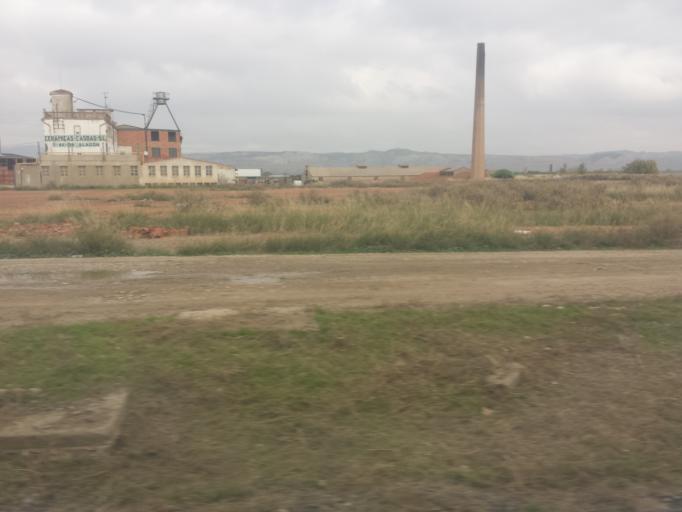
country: ES
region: Aragon
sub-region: Provincia de Zaragoza
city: Alagon
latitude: 41.7727
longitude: -1.1141
